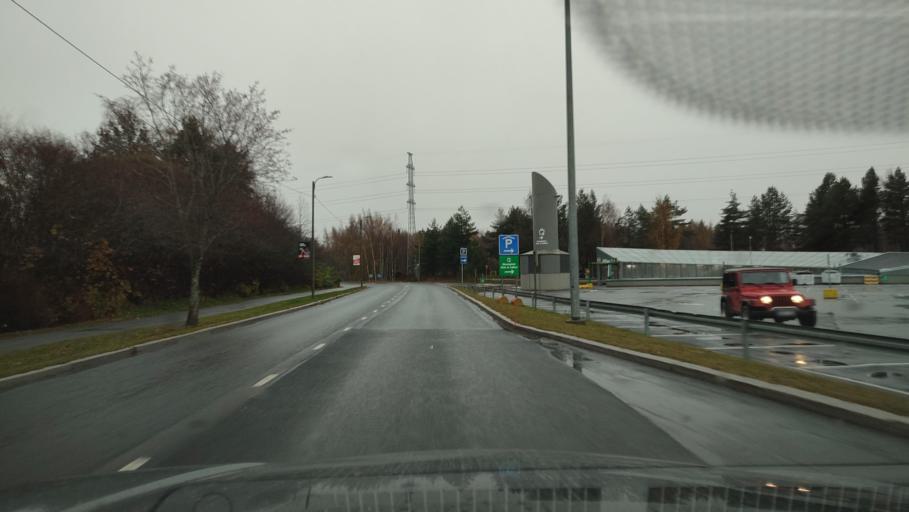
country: FI
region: Ostrobothnia
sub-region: Vaasa
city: Vaasa
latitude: 63.1023
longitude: 21.6475
